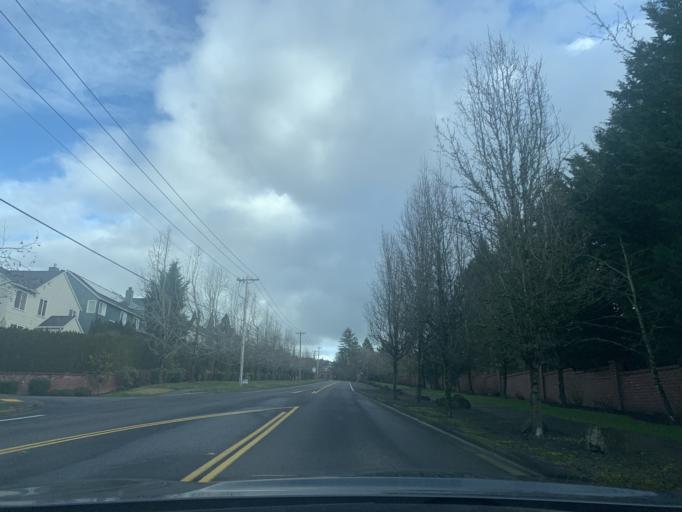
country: US
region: Oregon
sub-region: Washington County
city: Cedar Mill
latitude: 45.5484
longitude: -122.8093
